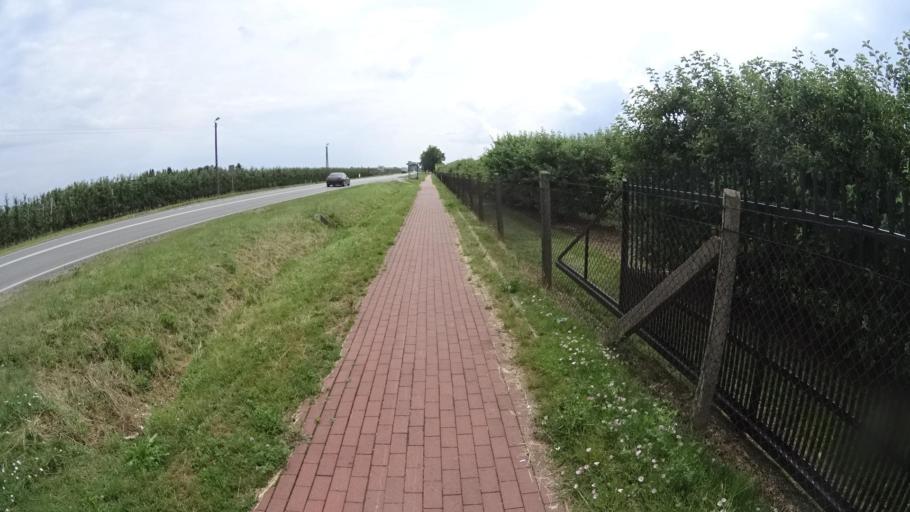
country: PL
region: Masovian Voivodeship
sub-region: Powiat grojecki
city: Grojec
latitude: 51.8875
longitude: 20.8630
